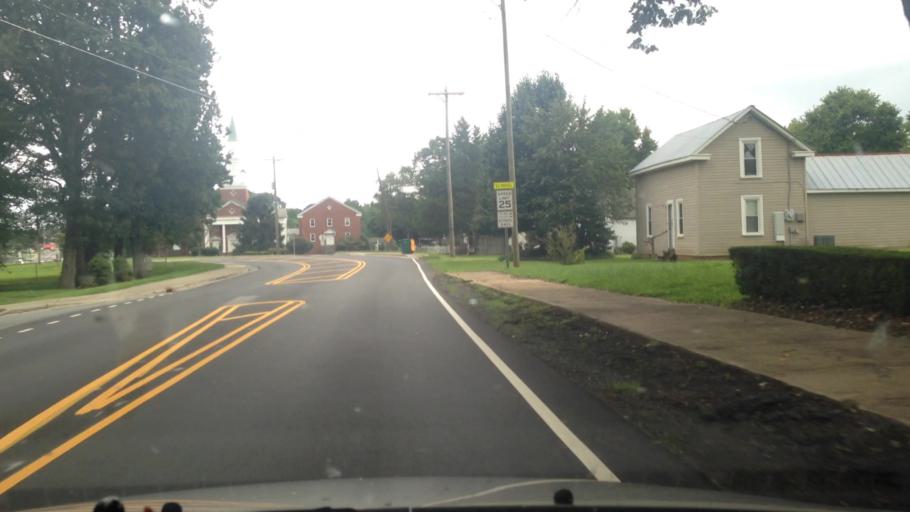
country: US
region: North Carolina
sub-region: Forsyth County
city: Walkertown
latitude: 36.1738
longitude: -80.1530
